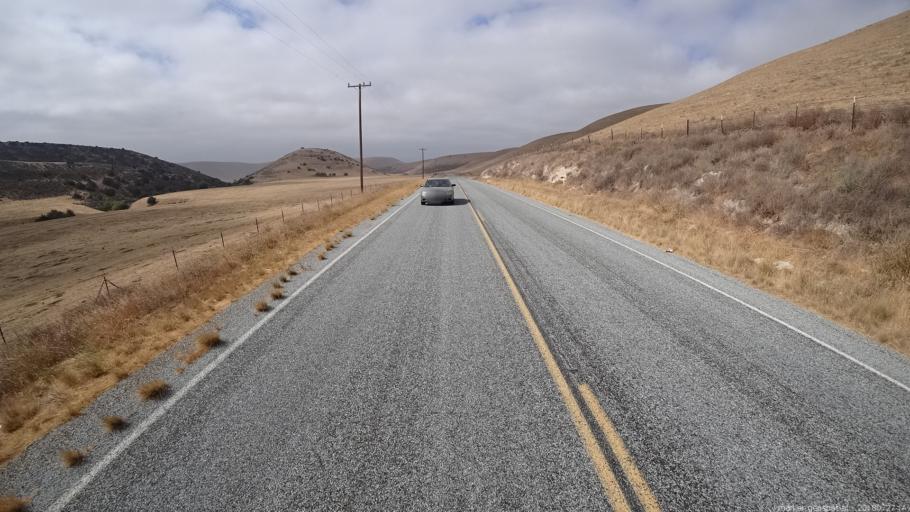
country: US
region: California
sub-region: Monterey County
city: King City
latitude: 36.2836
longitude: -121.0582
